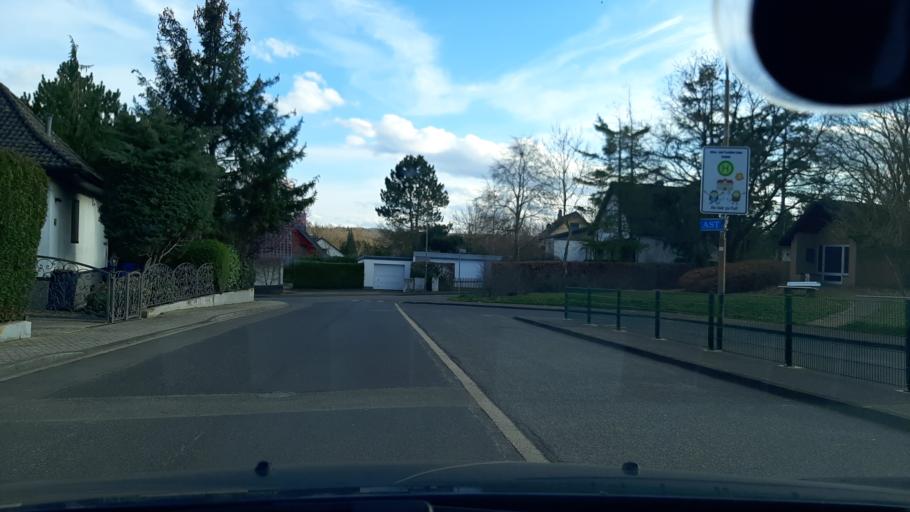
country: DE
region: North Rhine-Westphalia
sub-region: Regierungsbezirk Koln
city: Mechernich
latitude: 50.6196
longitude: 6.6998
